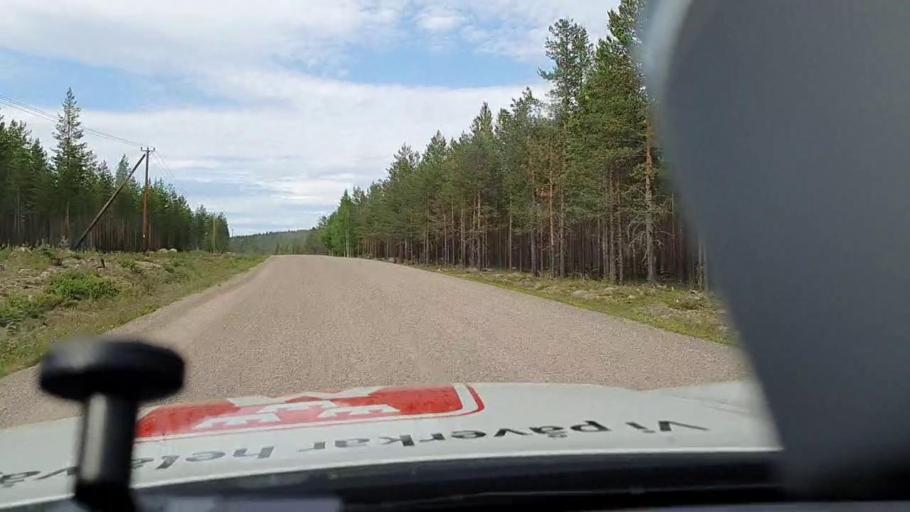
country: SE
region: Norrbotten
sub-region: Alvsbyns Kommun
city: AElvsbyn
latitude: 66.1230
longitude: 20.9933
